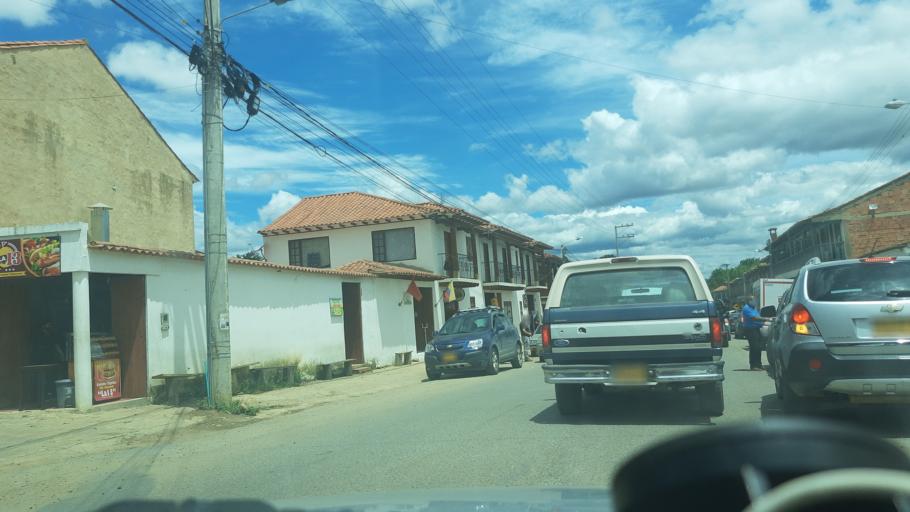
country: CO
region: Boyaca
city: Villa de Leiva
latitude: 5.6369
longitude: -73.5260
